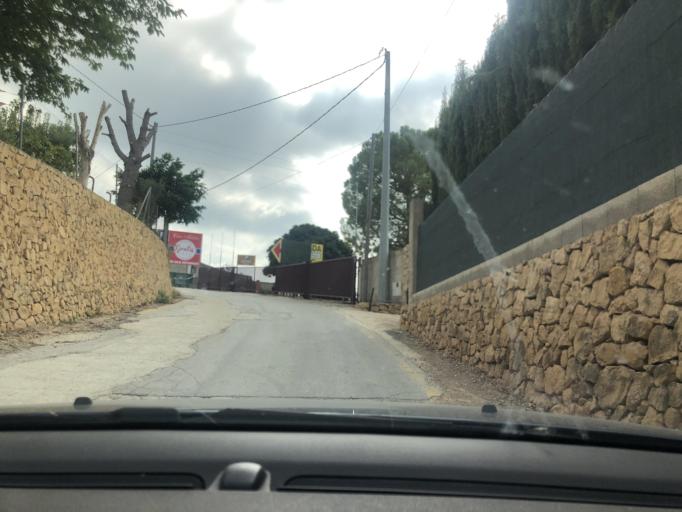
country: ES
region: Valencia
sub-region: Provincia de Alicante
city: Callosa d'En Sarria
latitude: 38.6579
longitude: -0.0953
